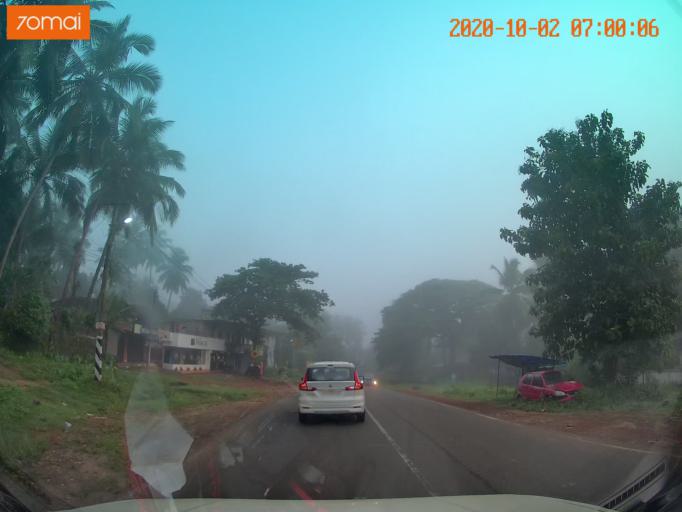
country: IN
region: Kerala
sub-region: Malappuram
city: Tirur
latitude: 10.8793
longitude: 76.0681
